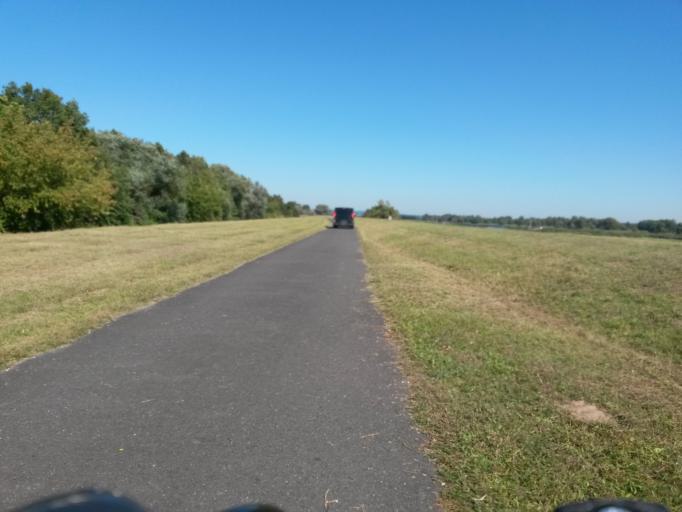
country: PL
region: West Pomeranian Voivodeship
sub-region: Powiat gryfinski
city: Cedynia
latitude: 52.8662
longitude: 14.1429
